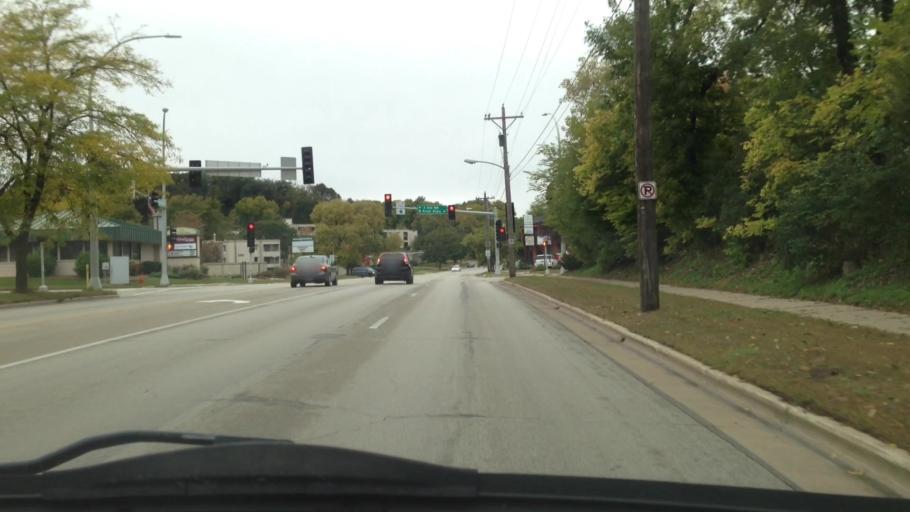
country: US
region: Minnesota
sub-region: Olmsted County
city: Rochester
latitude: 44.0442
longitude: -92.4669
